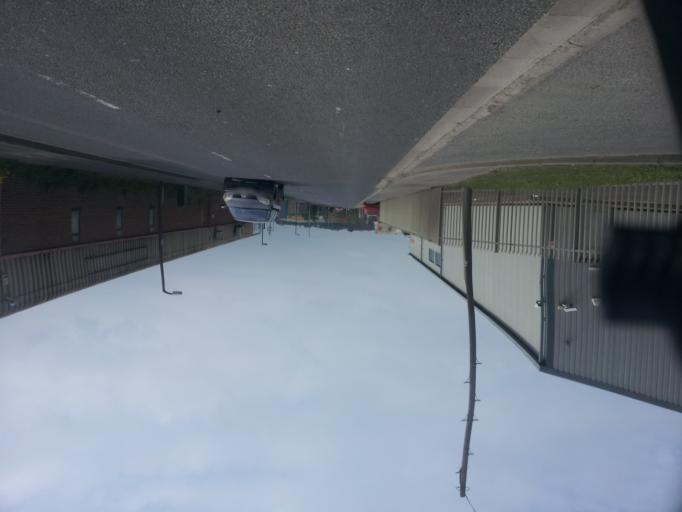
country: GB
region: England
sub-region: Medway
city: Rochester
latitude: 51.3974
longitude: 0.5127
